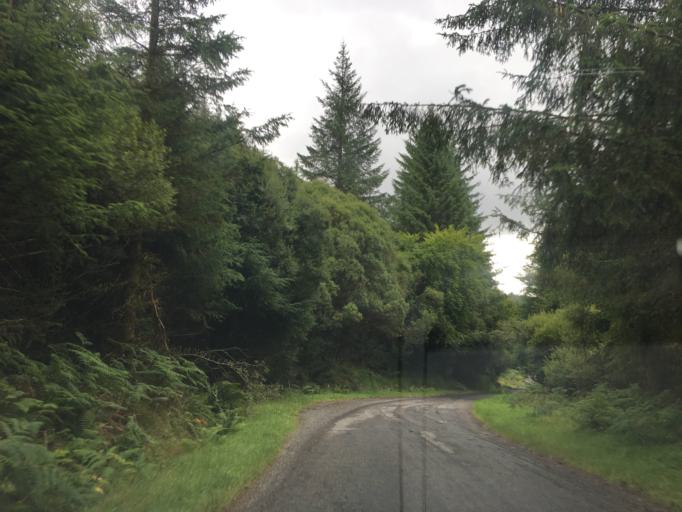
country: GB
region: Scotland
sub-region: Argyll and Bute
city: Oban
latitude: 56.2840
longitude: -5.2994
